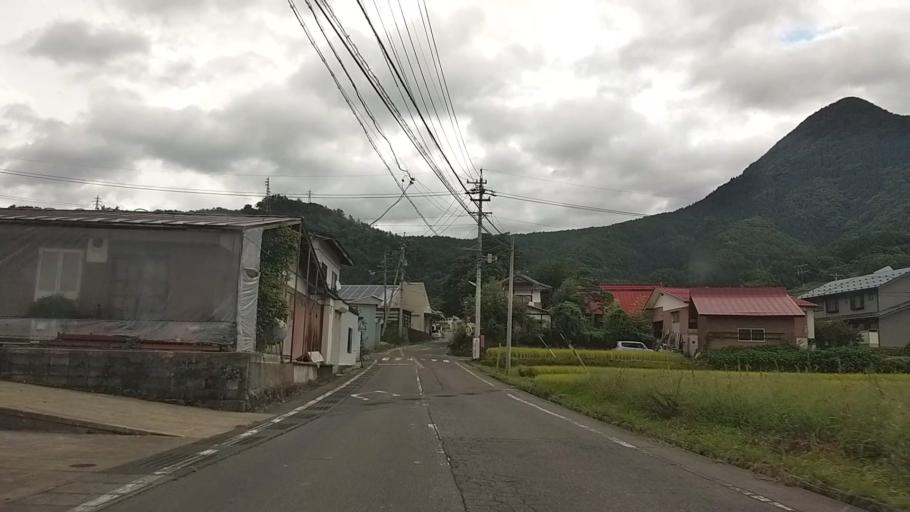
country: JP
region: Nagano
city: Iiyama
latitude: 36.8174
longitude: 138.3606
